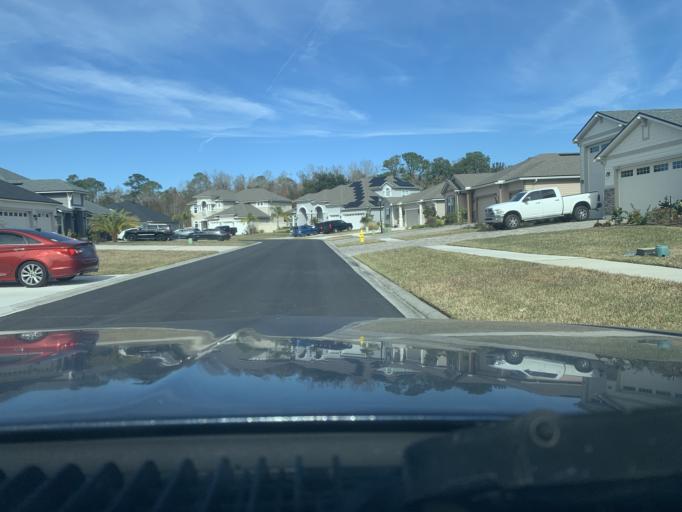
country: US
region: Florida
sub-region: Clay County
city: Green Cove Springs
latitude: 29.9785
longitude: -81.5287
